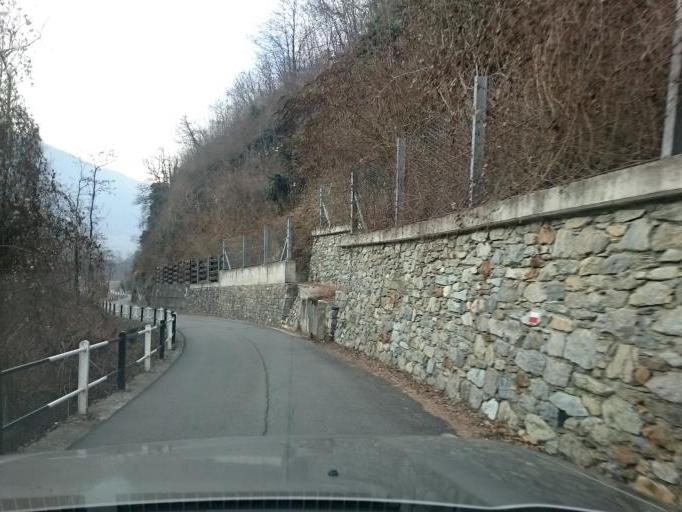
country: IT
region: Lombardy
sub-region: Provincia di Sondrio
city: Vervio
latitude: 46.2457
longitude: 10.2348
